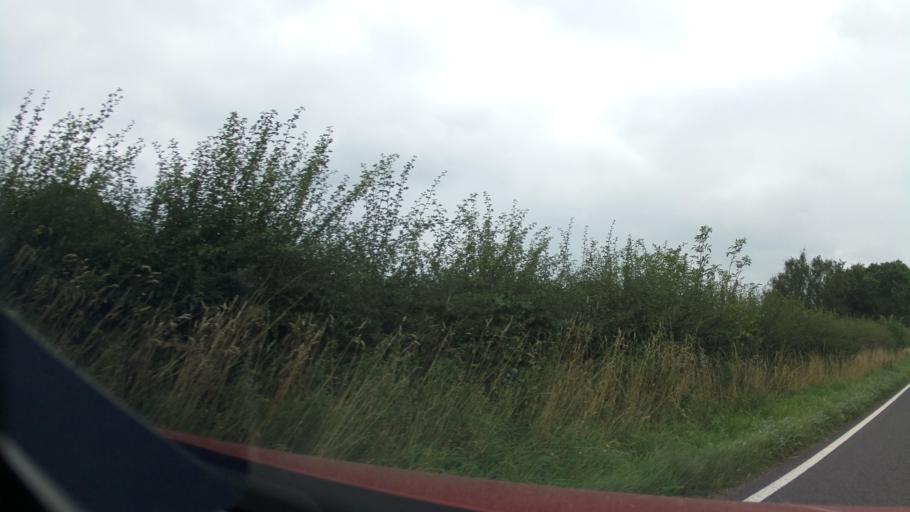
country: GB
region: England
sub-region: Derbyshire
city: Bradley
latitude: 53.0150
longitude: -1.6748
